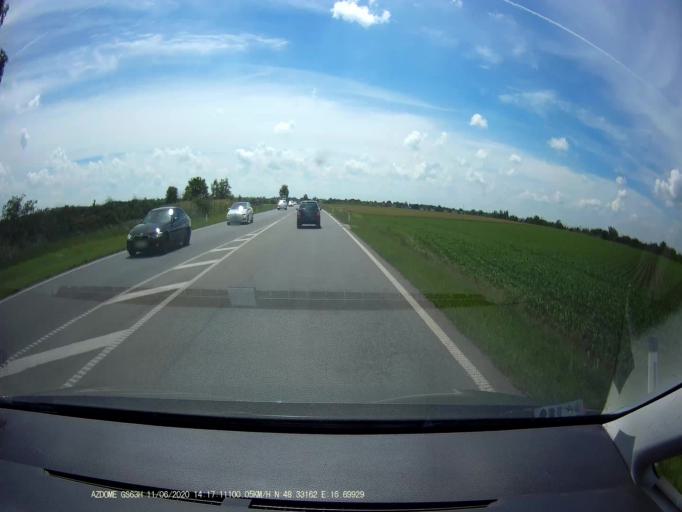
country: AT
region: Lower Austria
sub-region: Politischer Bezirk Ganserndorf
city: Ganserndorf
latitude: 48.3312
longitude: 16.6983
